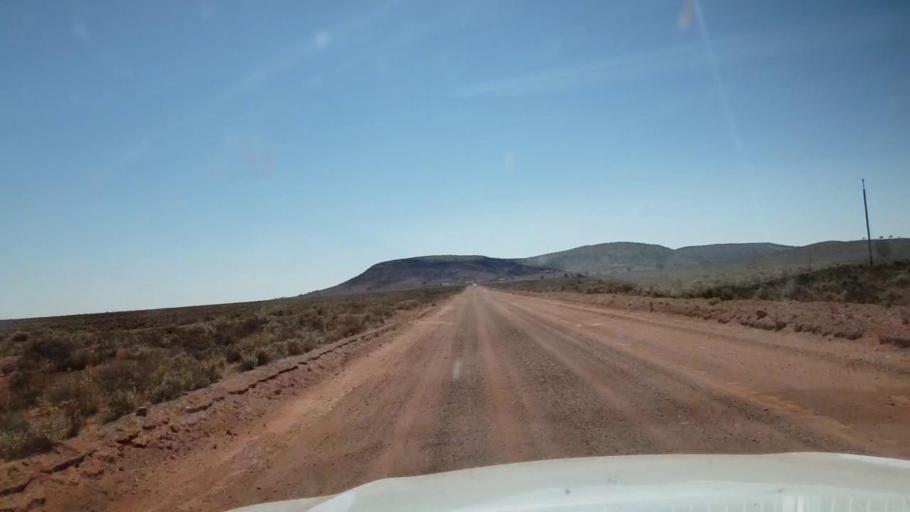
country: AU
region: South Australia
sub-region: Whyalla
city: Whyalla
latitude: -32.7041
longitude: 137.1363
